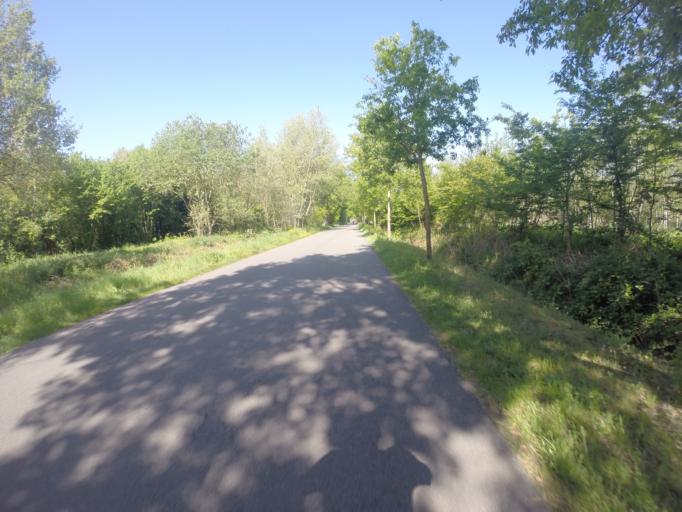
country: BE
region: Flanders
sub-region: Provincie Oost-Vlaanderen
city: Knesselare
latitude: 51.1635
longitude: 3.4242
